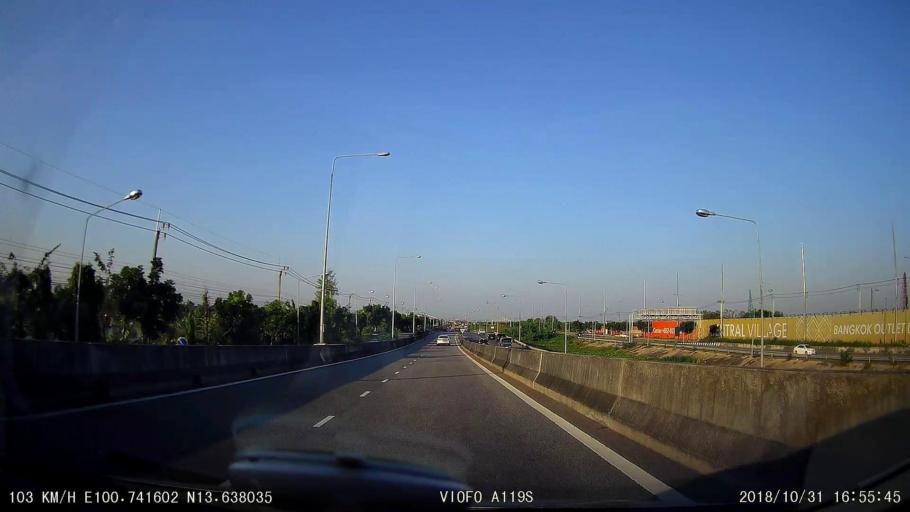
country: TH
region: Samut Prakan
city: Ban Khlong Bang Sao Thong
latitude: 13.6381
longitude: 100.7416
